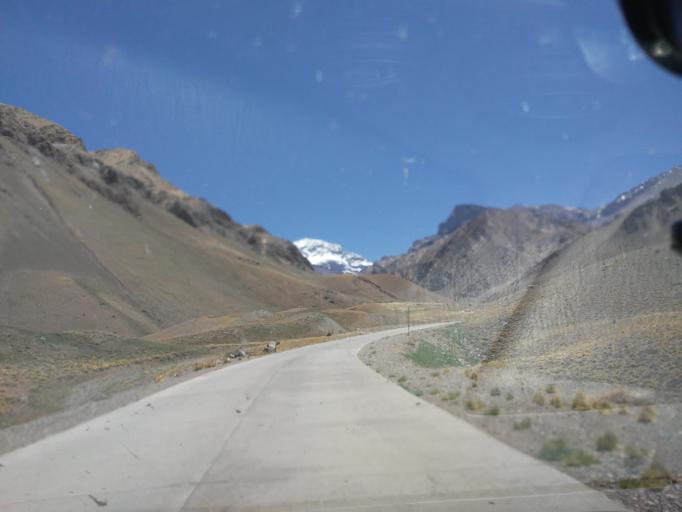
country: CL
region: Valparaiso
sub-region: Provincia de Los Andes
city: Los Andes
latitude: -32.8173
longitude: -69.9425
